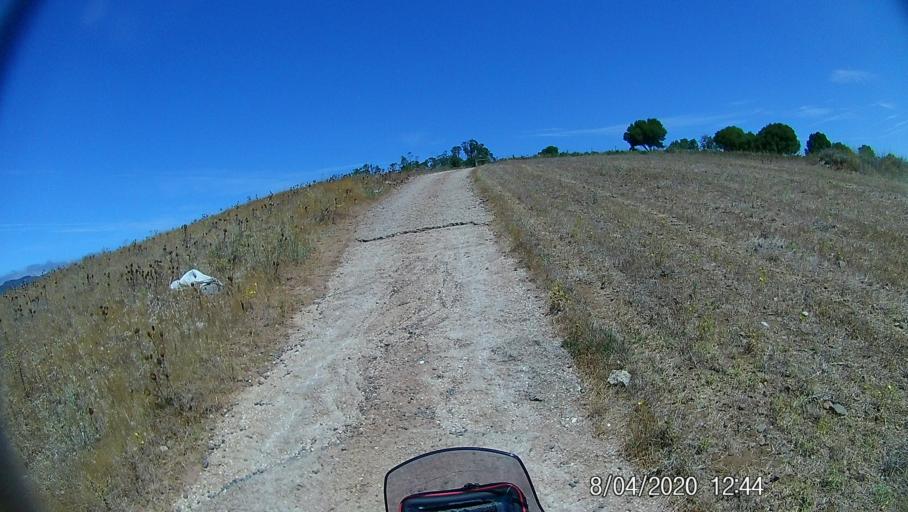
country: PT
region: Lisbon
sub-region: Cascais
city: Alcabideche
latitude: 38.7434
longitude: -9.3651
